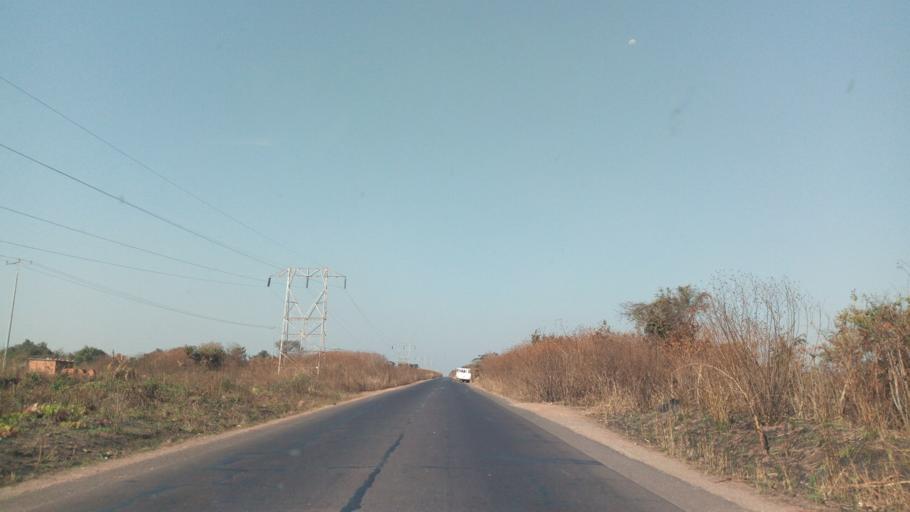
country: CD
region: Katanga
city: Likasi
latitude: -11.0019
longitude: 26.8622
